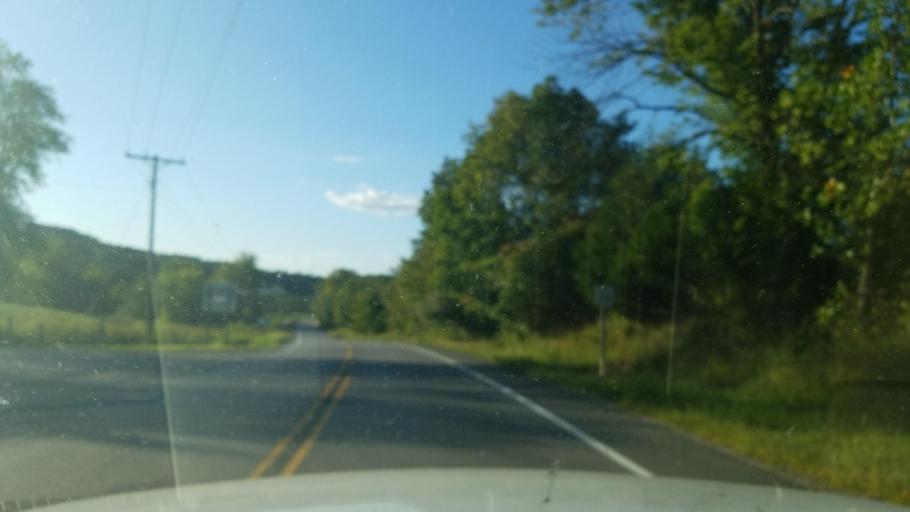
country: US
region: Illinois
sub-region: Hardin County
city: Rosiclare
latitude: 37.5645
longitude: -88.4094
